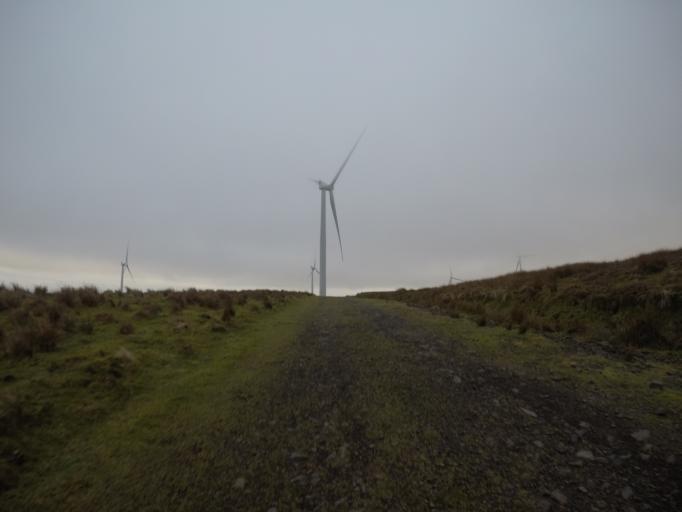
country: GB
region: Scotland
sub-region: North Ayrshire
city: Dalry
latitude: 55.7379
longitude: -4.7777
